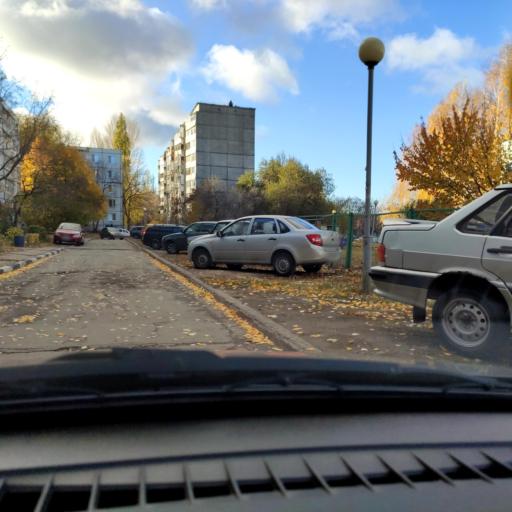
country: RU
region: Samara
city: Tol'yatti
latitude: 53.5319
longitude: 49.3114
